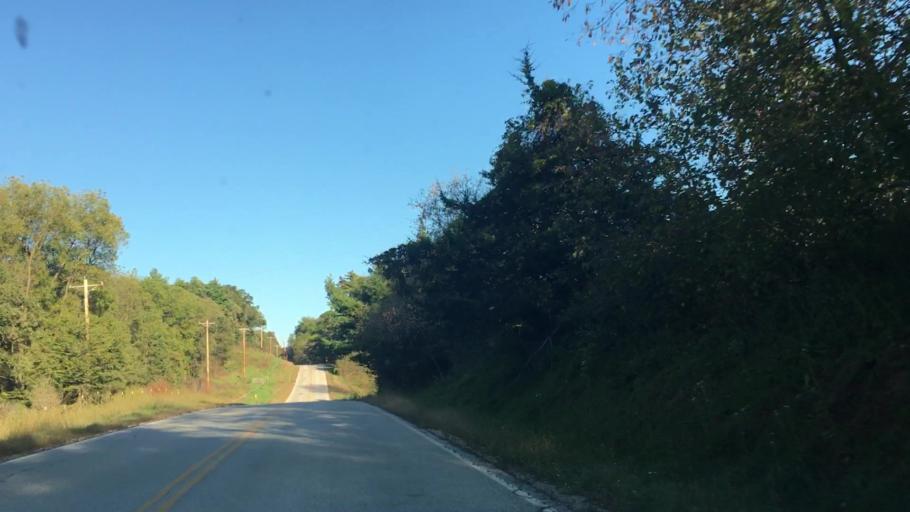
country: US
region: Minnesota
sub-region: Fillmore County
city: Chatfield
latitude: 43.8182
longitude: -92.0475
